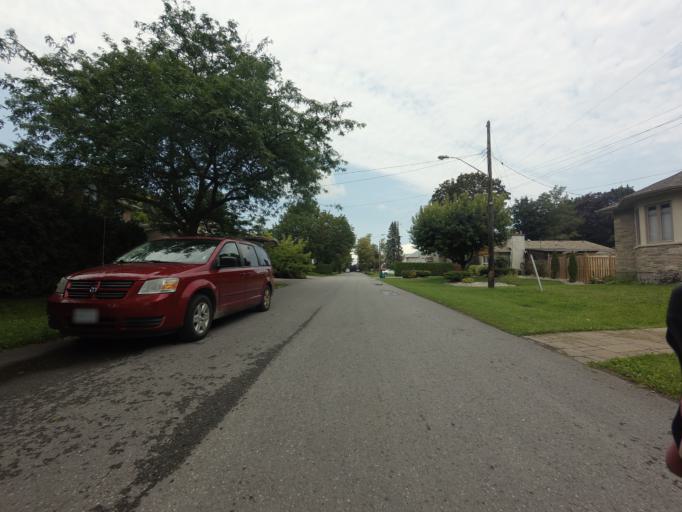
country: CA
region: Ontario
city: Ottawa
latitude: 45.3591
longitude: -75.7071
